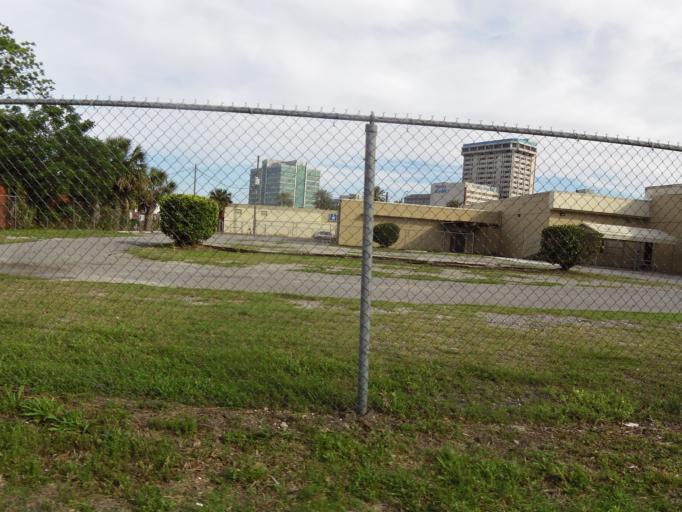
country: US
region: Florida
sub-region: Duval County
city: Jacksonville
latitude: 30.3234
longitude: -81.6771
